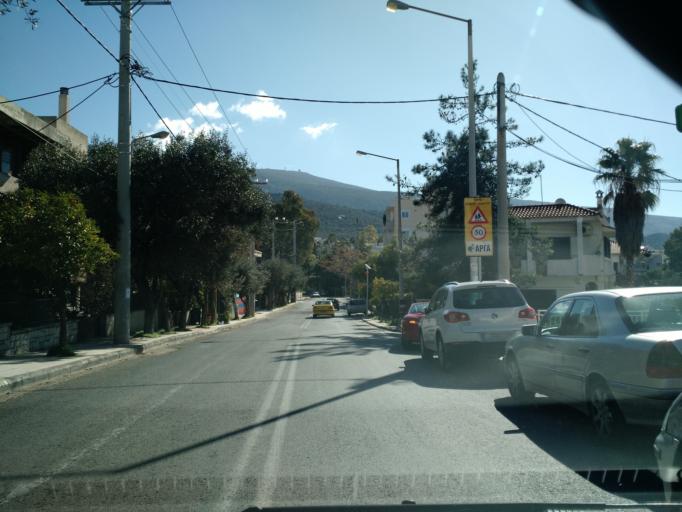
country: GR
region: Attica
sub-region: Nomarchia Athinas
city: Papagou
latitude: 37.9857
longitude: 23.7931
